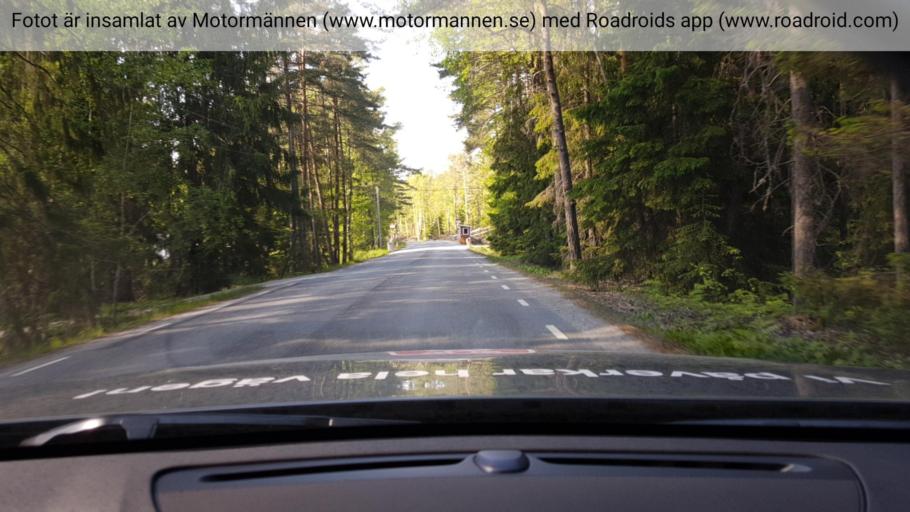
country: SE
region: Stockholm
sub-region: Varmdo Kommun
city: Mortnas
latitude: 59.2672
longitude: 18.4284
